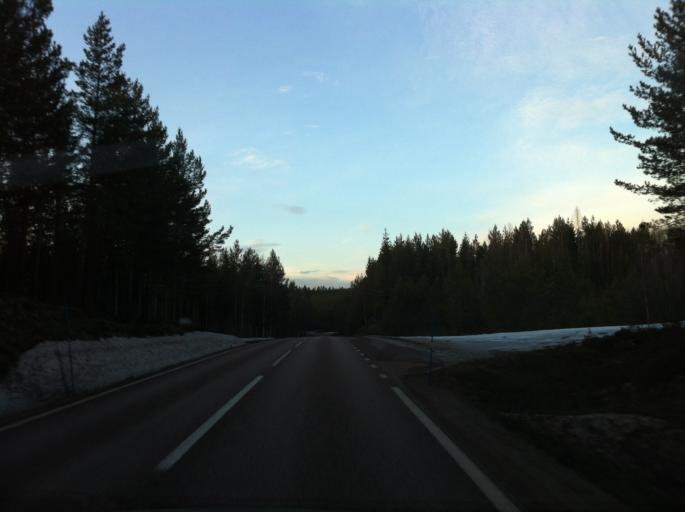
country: SE
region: Dalarna
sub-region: Vansbro Kommun
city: Vansbro
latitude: 60.5625
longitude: 14.1947
